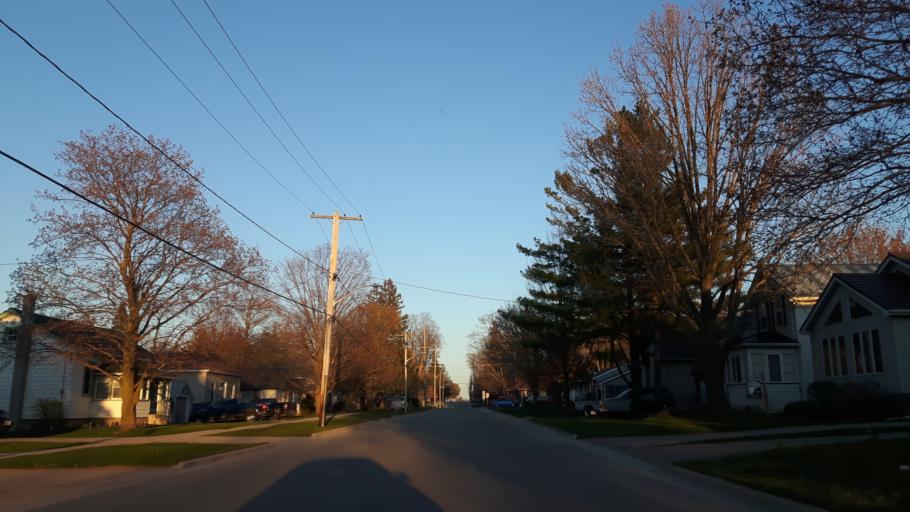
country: CA
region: Ontario
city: Bluewater
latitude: 43.6183
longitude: -81.5376
